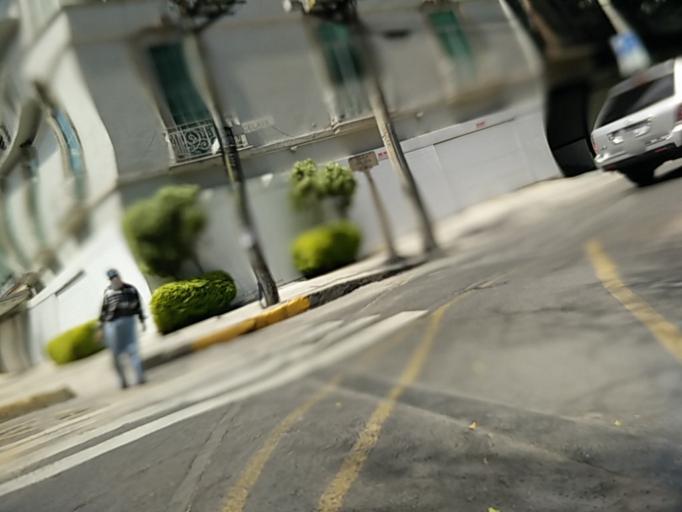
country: MX
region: Mexico City
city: Benito Juarez
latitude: 19.4139
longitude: -99.1660
